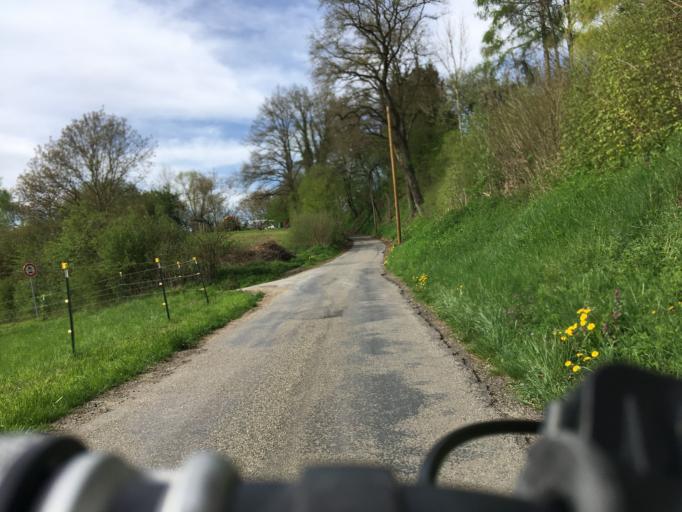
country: DE
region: Baden-Wuerttemberg
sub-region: Freiburg Region
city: Hilzingen
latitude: 47.7517
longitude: 8.7978
